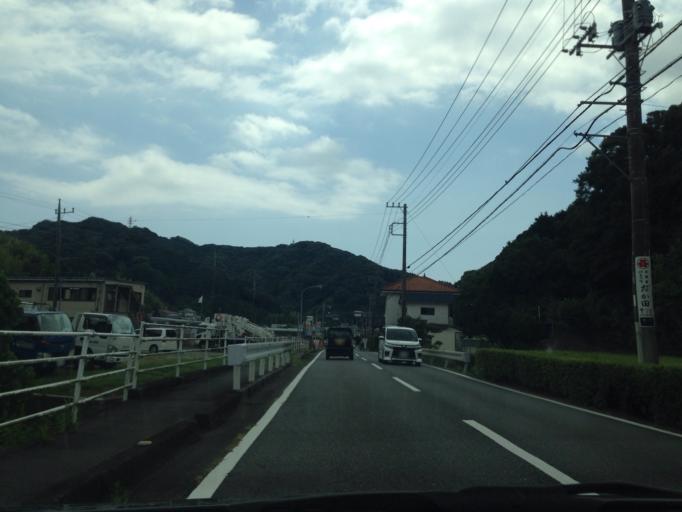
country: JP
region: Shizuoka
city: Shimoda
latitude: 34.6599
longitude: 138.8902
